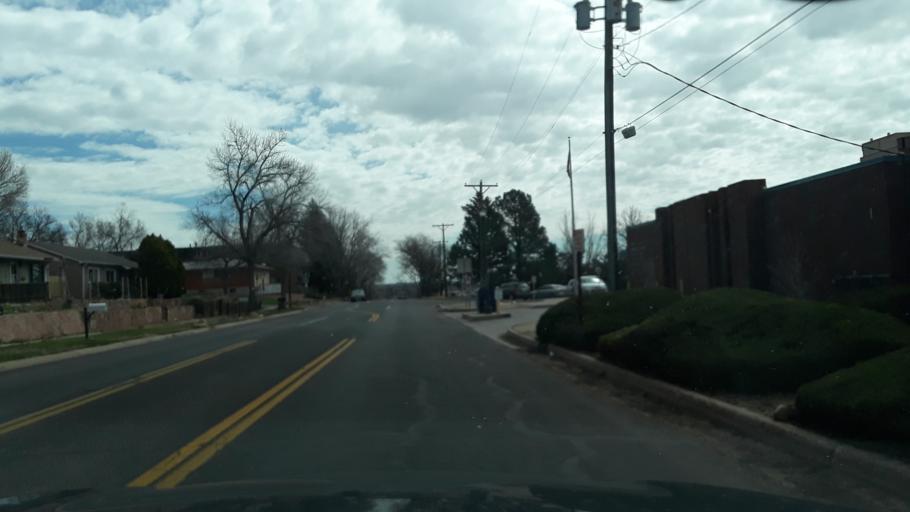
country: US
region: Colorado
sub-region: El Paso County
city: Colorado Springs
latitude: 38.8489
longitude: -104.7792
